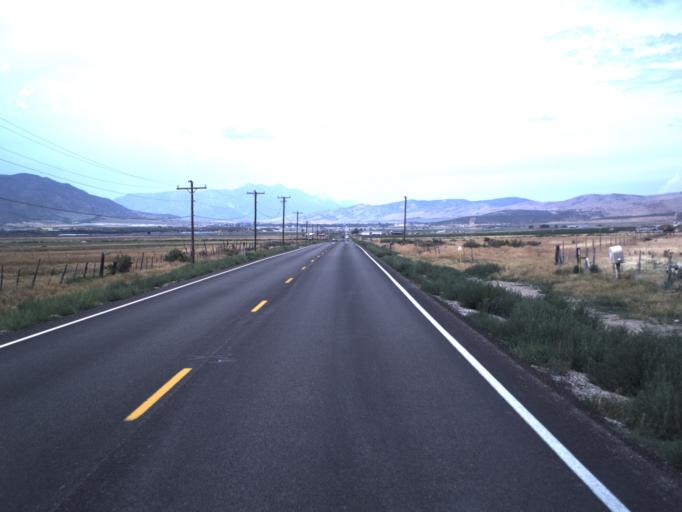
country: US
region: Utah
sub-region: Sanpete County
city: Moroni
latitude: 39.5608
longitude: -111.6022
